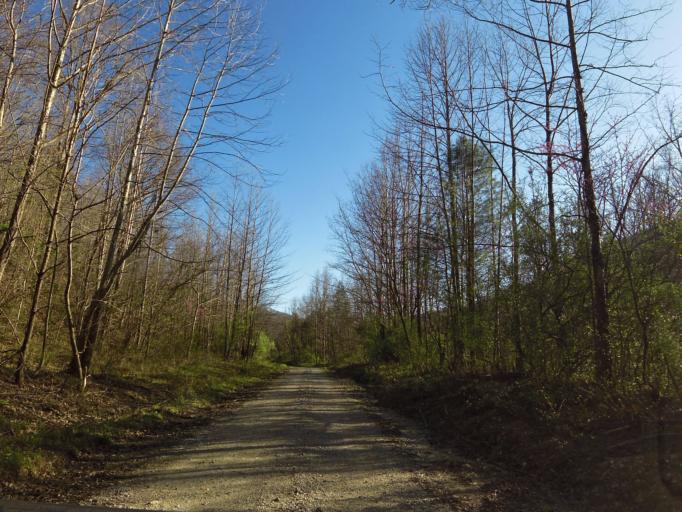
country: US
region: Tennessee
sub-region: Roane County
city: Oliver Springs
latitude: 36.2124
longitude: -84.4155
